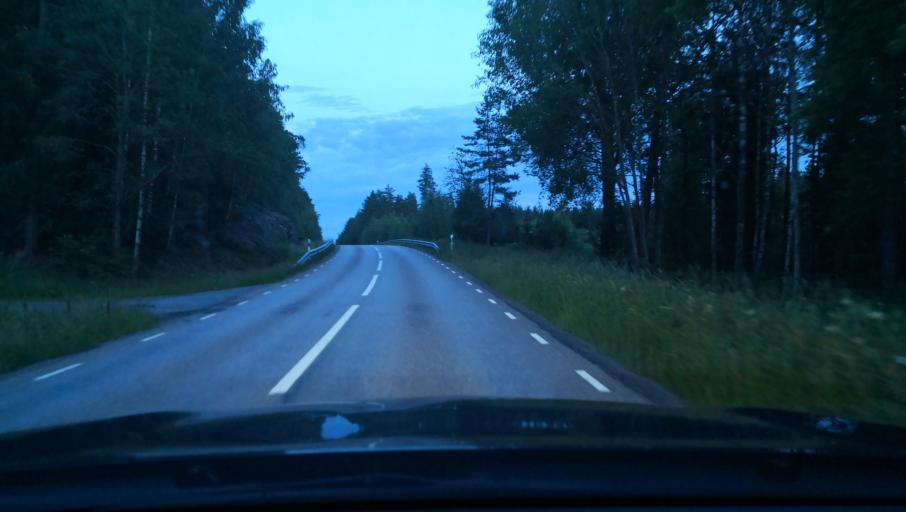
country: SE
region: Uppsala
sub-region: Heby Kommun
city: OEstervala
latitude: 60.0075
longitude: 17.2967
